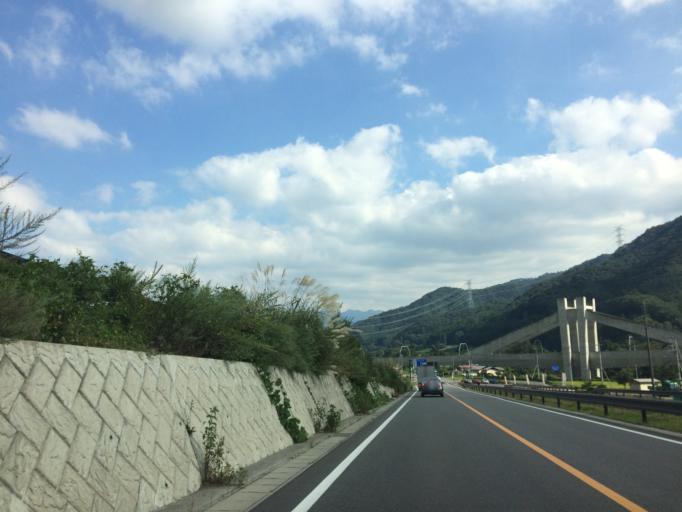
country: JP
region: Gunma
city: Nakanojomachi
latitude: 36.5702
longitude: 138.7448
